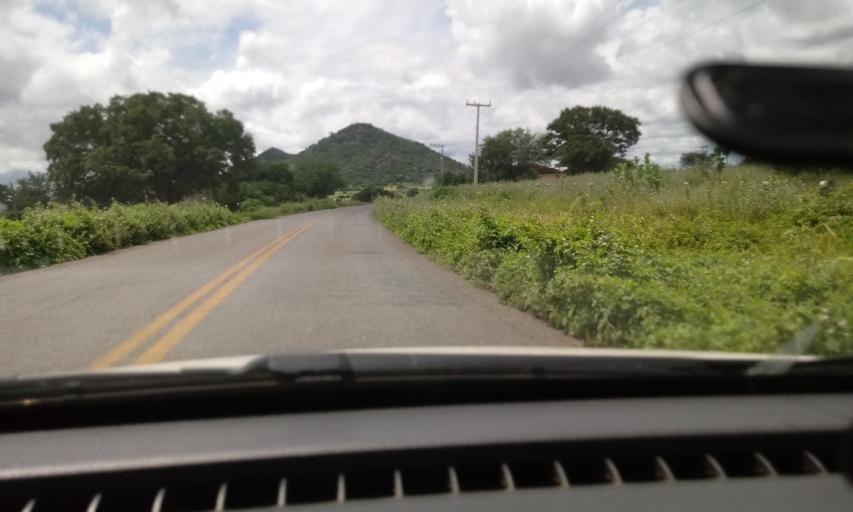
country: BR
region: Bahia
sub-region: Guanambi
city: Guanambi
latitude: -14.0741
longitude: -42.8795
